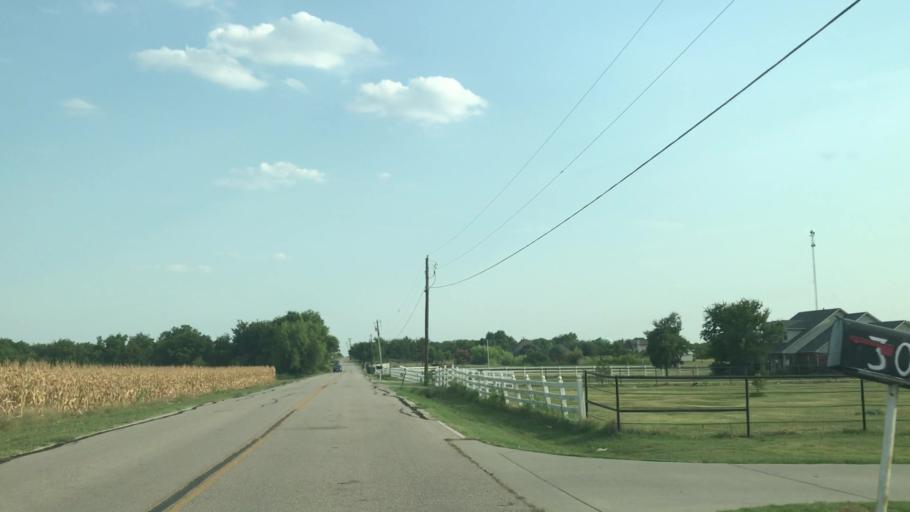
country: US
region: Texas
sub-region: Rockwall County
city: Fate
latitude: 32.9315
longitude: -96.4009
